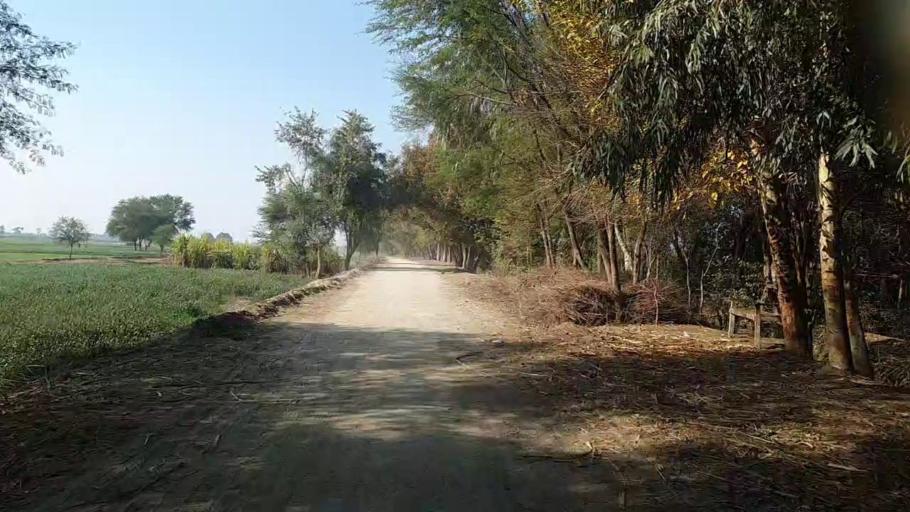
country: PK
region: Sindh
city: Mirpur Mathelo
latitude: 27.8976
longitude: 69.6509
